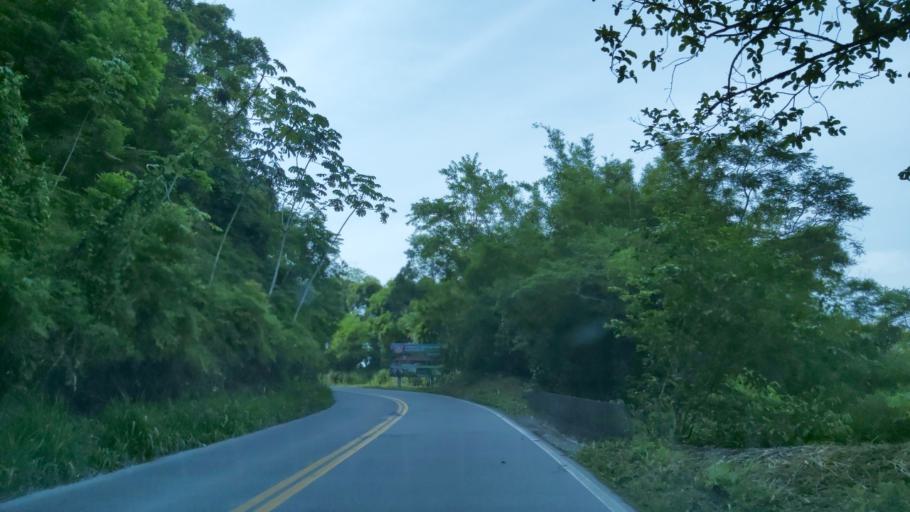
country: BR
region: Sao Paulo
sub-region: Juquia
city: Juquia
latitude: -24.1100
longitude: -47.6284
